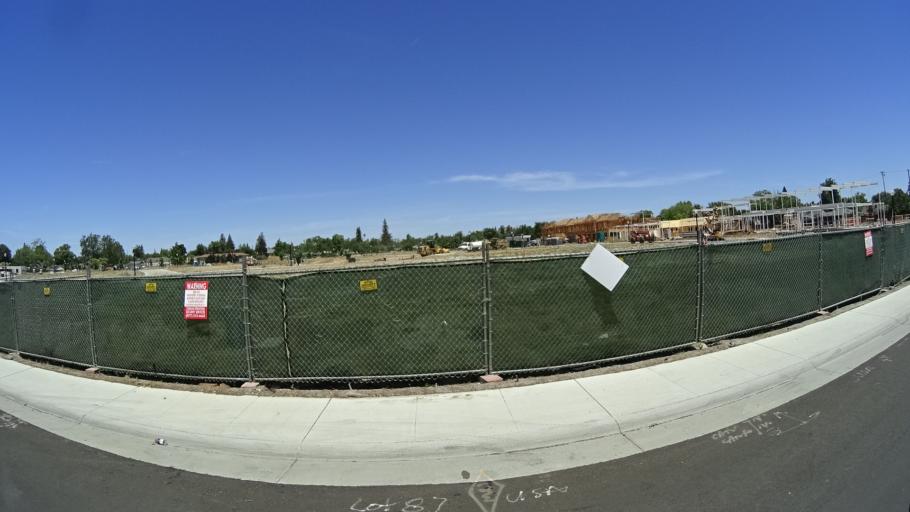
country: US
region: California
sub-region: Sacramento County
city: Sacramento
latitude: 38.5705
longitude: -121.4377
